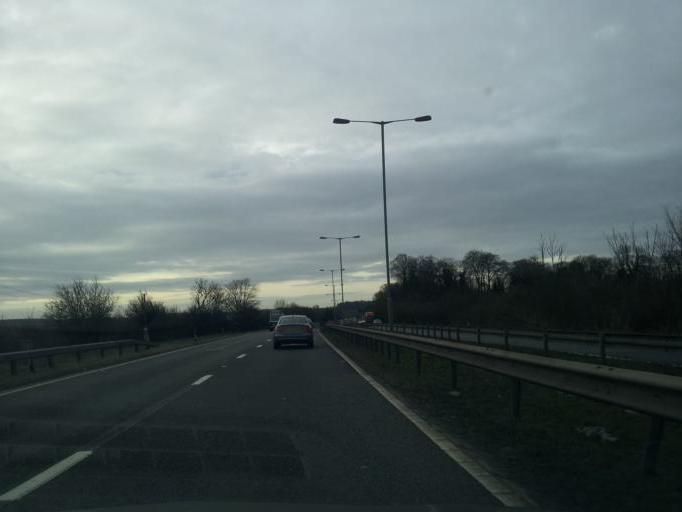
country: GB
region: England
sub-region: Lincolnshire
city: Grantham
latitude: 52.8701
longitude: -0.6301
